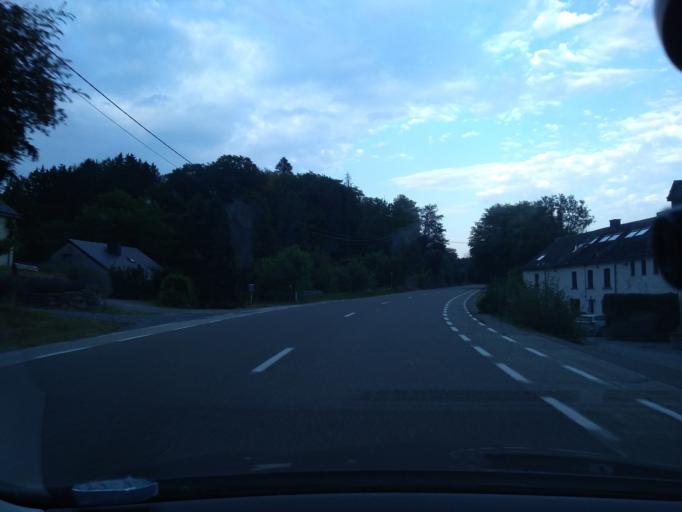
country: BE
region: Wallonia
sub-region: Province du Luxembourg
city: Saint-Hubert
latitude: 50.0218
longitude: 5.3416
